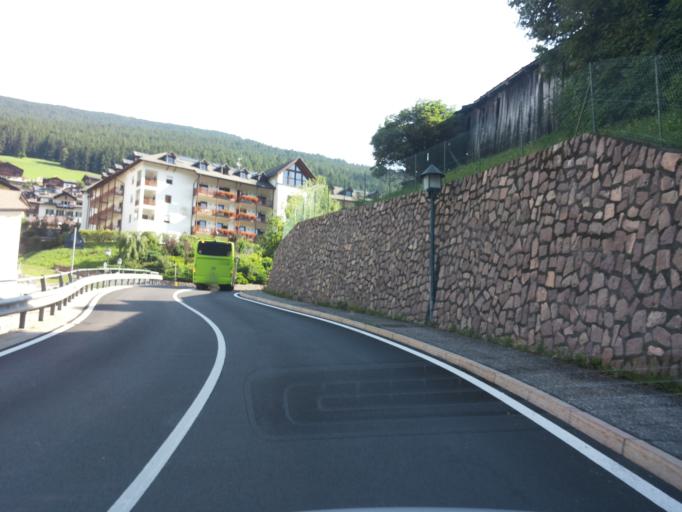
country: IT
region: Trentino-Alto Adige
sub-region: Bolzano
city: Ortisei
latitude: 46.5744
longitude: 11.6678
